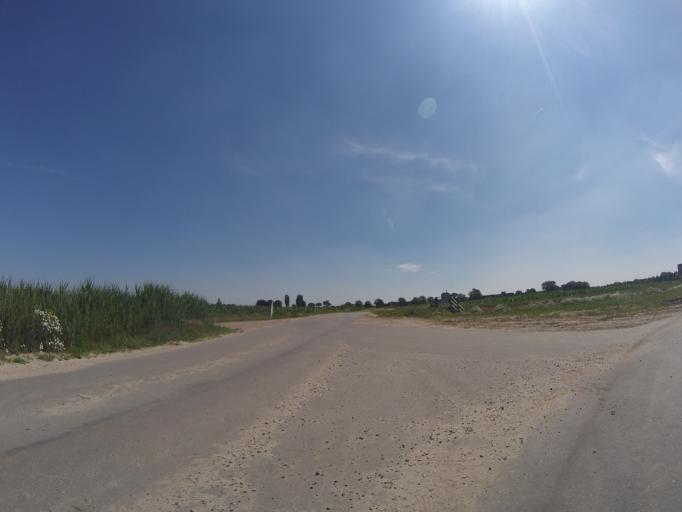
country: NL
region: Utrecht
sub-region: Gemeente Amersfoort
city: Hoogland
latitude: 52.2062
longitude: 5.4106
